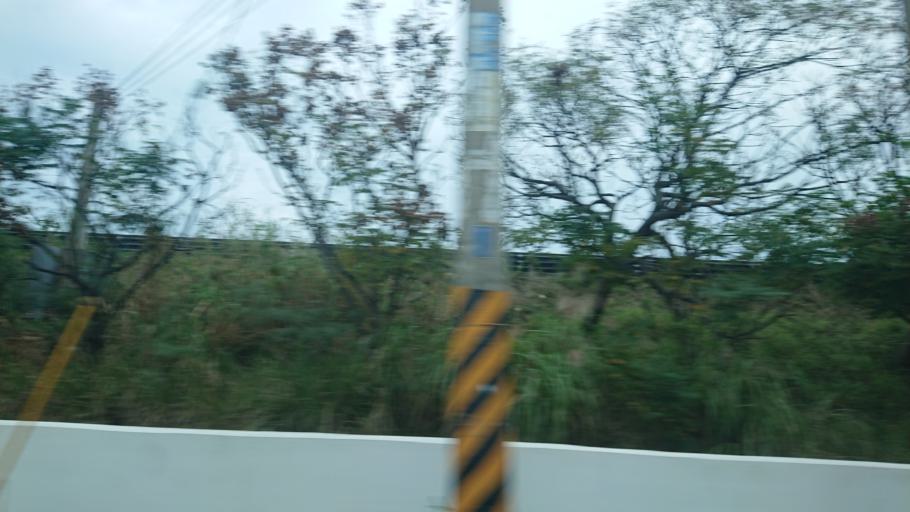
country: TW
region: Taiwan
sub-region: Hsinchu
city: Hsinchu
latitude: 24.8395
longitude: 120.9421
